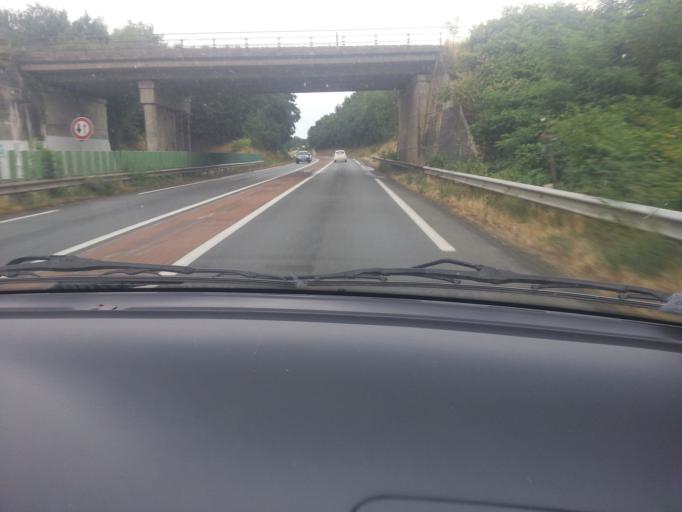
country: FR
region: Bourgogne
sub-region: Departement de Saone-et-Loire
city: Blanzy
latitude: 46.7004
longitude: 4.4003
